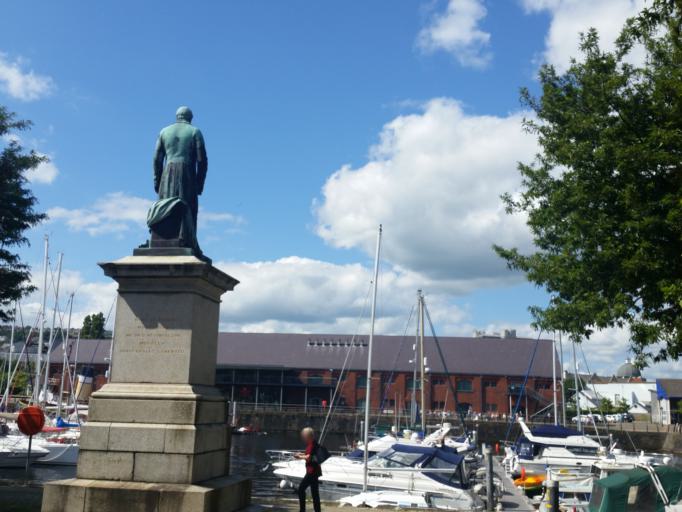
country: GB
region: Wales
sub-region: City and County of Swansea
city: Swansea
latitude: 51.6153
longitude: -3.9375
